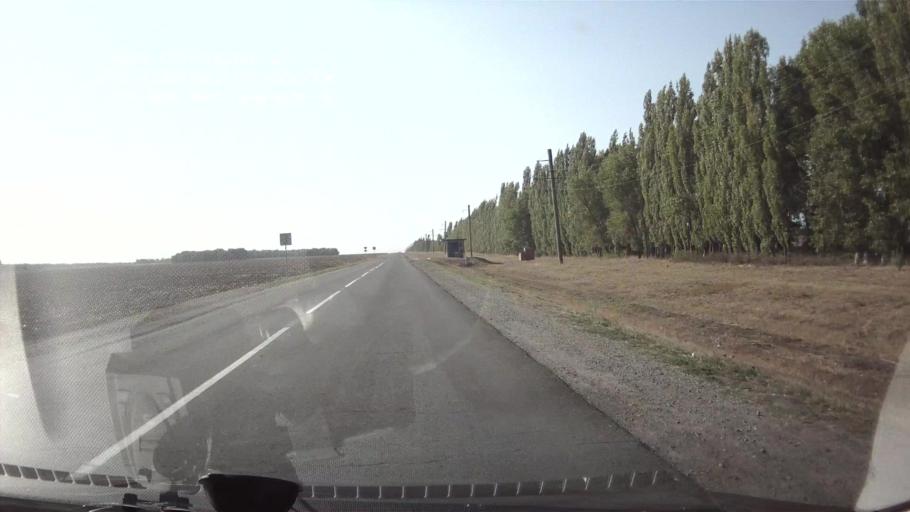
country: RU
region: Rostov
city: Tselina
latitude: 46.5361
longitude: 40.8998
